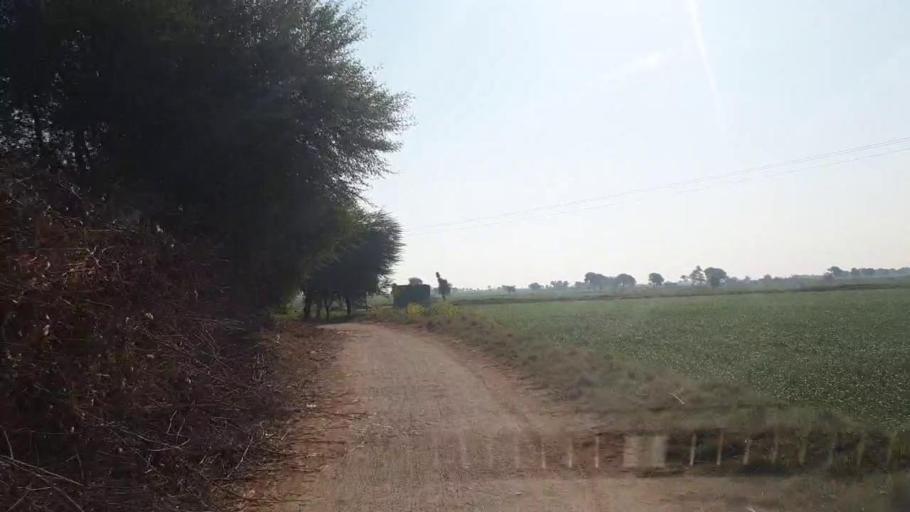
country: PK
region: Sindh
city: Shahpur Chakar
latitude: 26.0829
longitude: 68.5937
